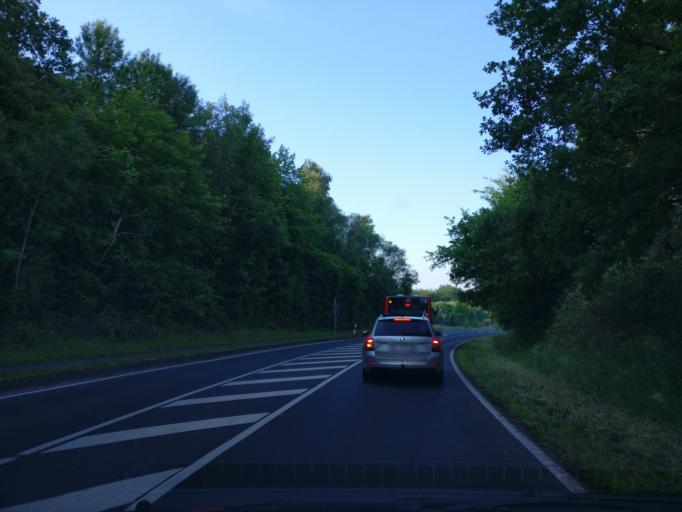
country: DE
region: Hesse
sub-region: Regierungsbezirk Kassel
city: Baunatal
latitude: 51.2736
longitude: 9.3999
